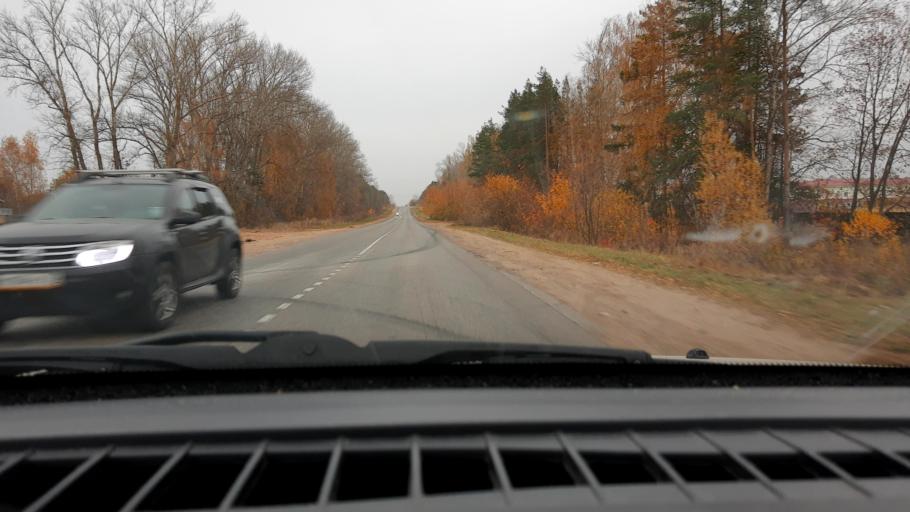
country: RU
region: Nizjnij Novgorod
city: Burevestnik
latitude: 56.0611
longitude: 43.8734
